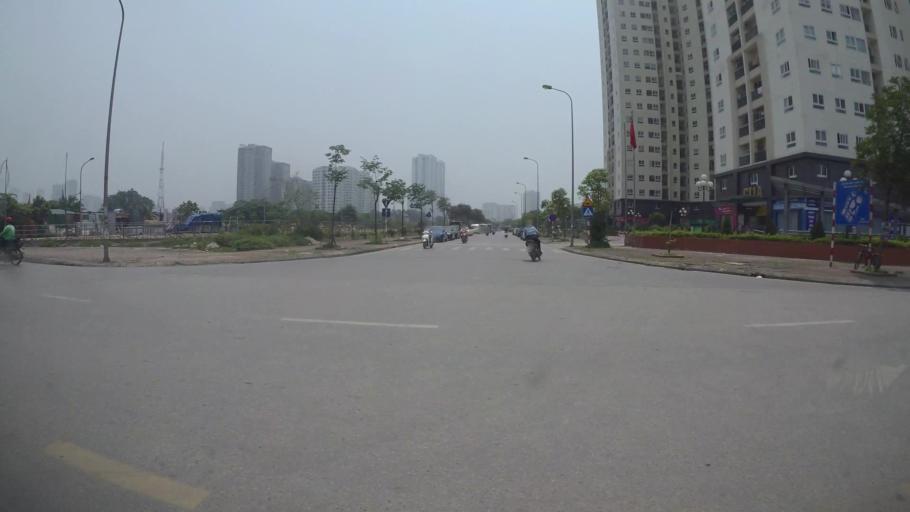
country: VN
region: Ha Noi
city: Thanh Xuan
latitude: 20.9960
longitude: 105.7790
